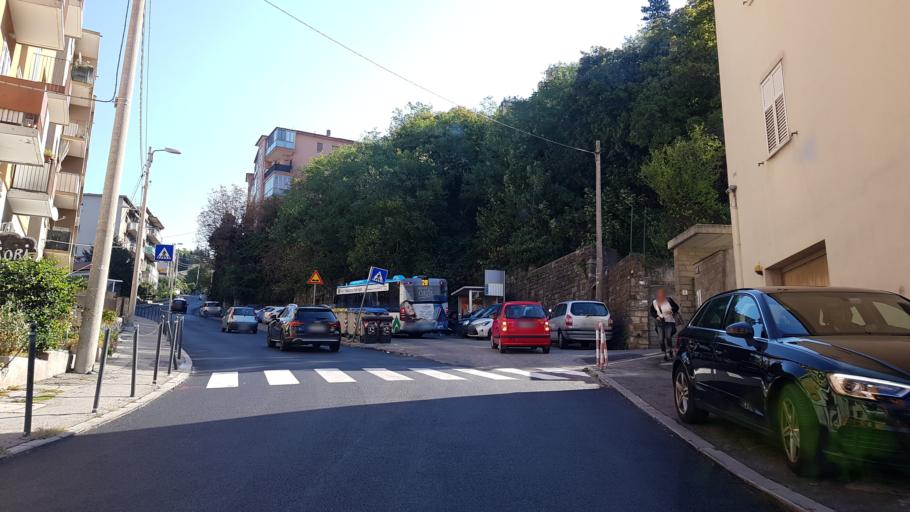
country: IT
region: Friuli Venezia Giulia
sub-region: Provincia di Trieste
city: Trieste
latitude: 45.6641
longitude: 13.7801
